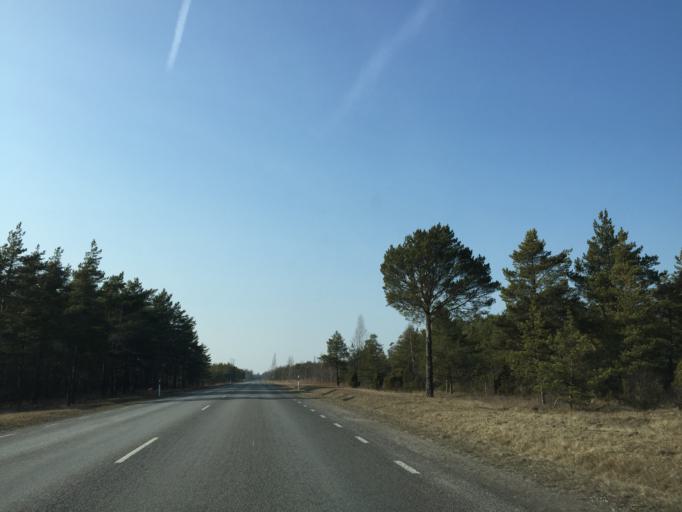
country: EE
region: Saare
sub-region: Orissaare vald
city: Orissaare
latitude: 58.5769
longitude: 23.3689
